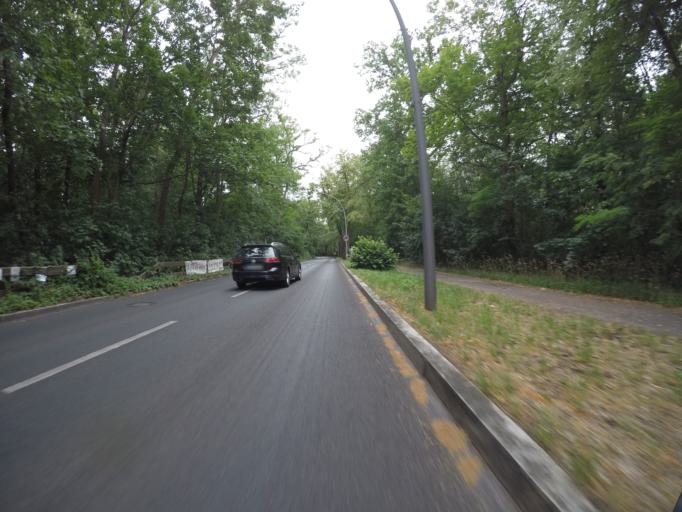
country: DE
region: Brandenburg
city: Teltow
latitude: 52.4142
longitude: 13.2724
